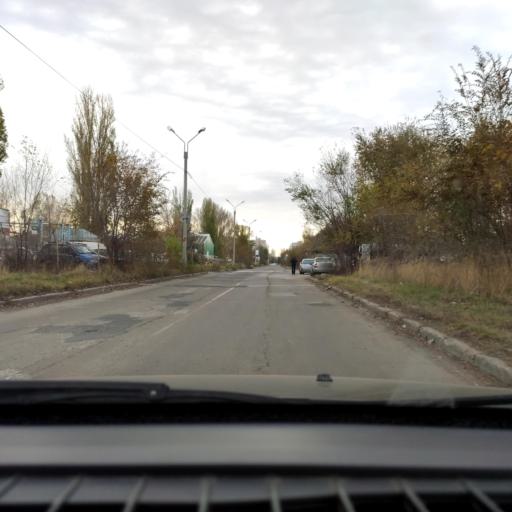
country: RU
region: Samara
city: Tol'yatti
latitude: 53.5550
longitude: 49.3140
